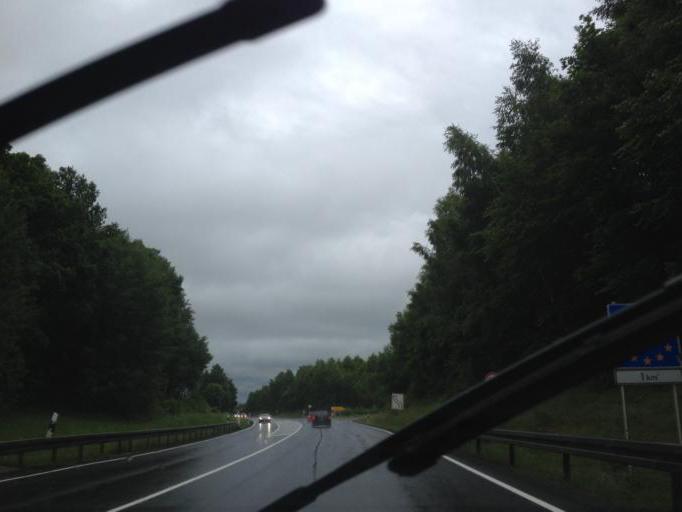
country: DE
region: Bavaria
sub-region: Upper Franconia
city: Schirnding
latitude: 50.0844
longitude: 12.2372
